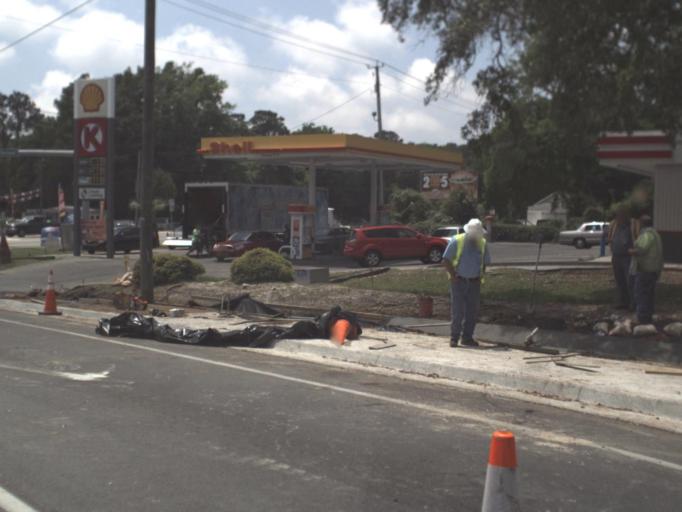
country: US
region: Florida
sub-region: Escambia County
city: Warrington
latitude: 30.3813
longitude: -87.3085
